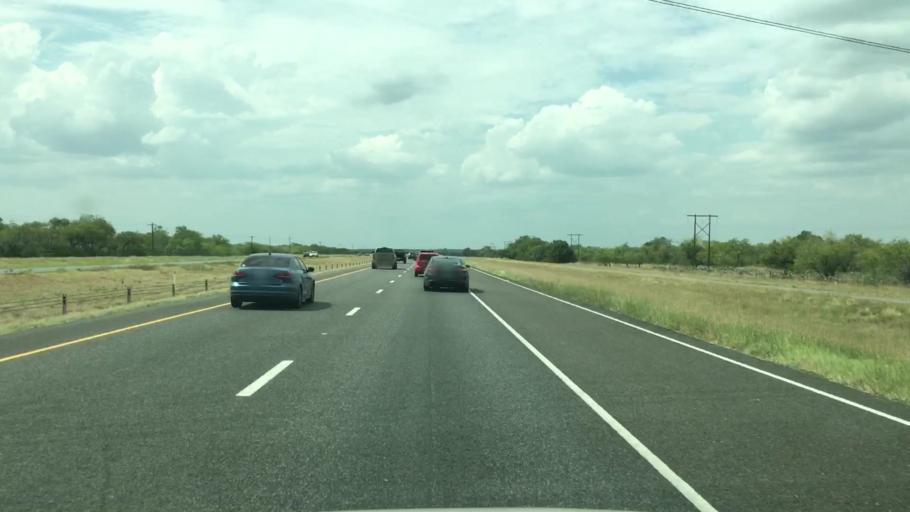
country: US
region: Texas
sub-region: Atascosa County
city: Pleasanton
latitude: 28.8217
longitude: -98.3621
